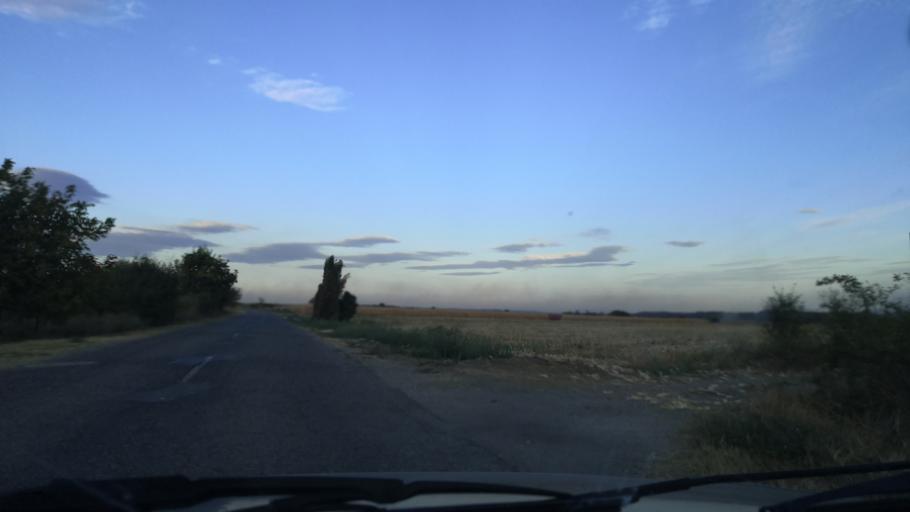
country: RS
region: Central Serbia
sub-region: Borski Okrug
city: Negotin
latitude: 44.2405
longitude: 22.5607
